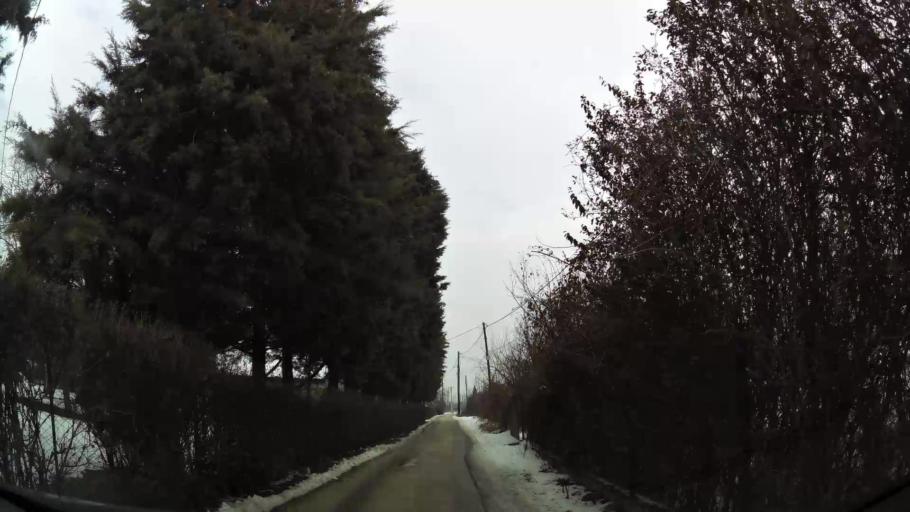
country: MK
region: Saraj
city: Saraj
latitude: 42.0492
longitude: 21.3593
